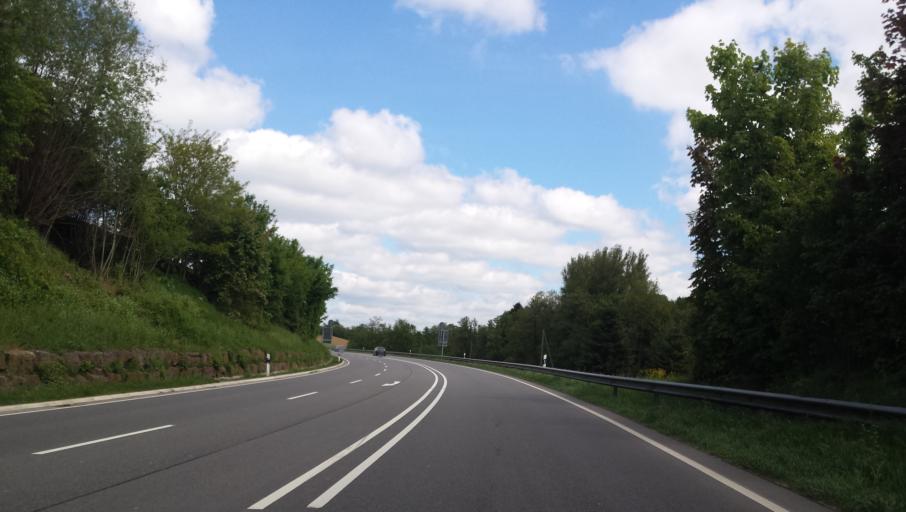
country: DE
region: Baden-Wuerttemberg
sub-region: Karlsruhe Region
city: Aglasterhausen
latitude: 49.3423
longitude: 8.9769
